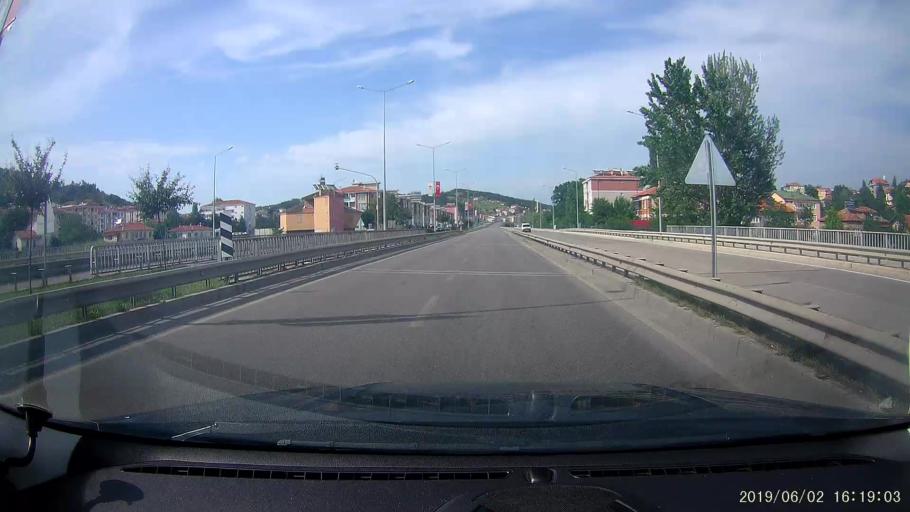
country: TR
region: Samsun
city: Havza
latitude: 40.9627
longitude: 35.6668
